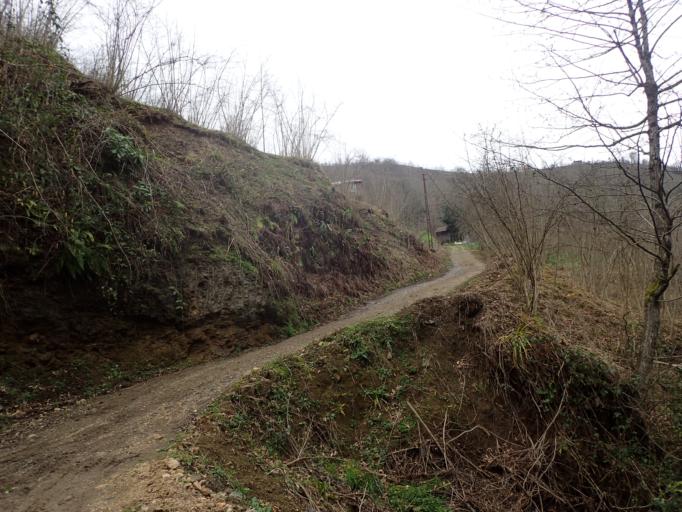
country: TR
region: Ordu
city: Camas
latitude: 40.8880
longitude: 37.5062
